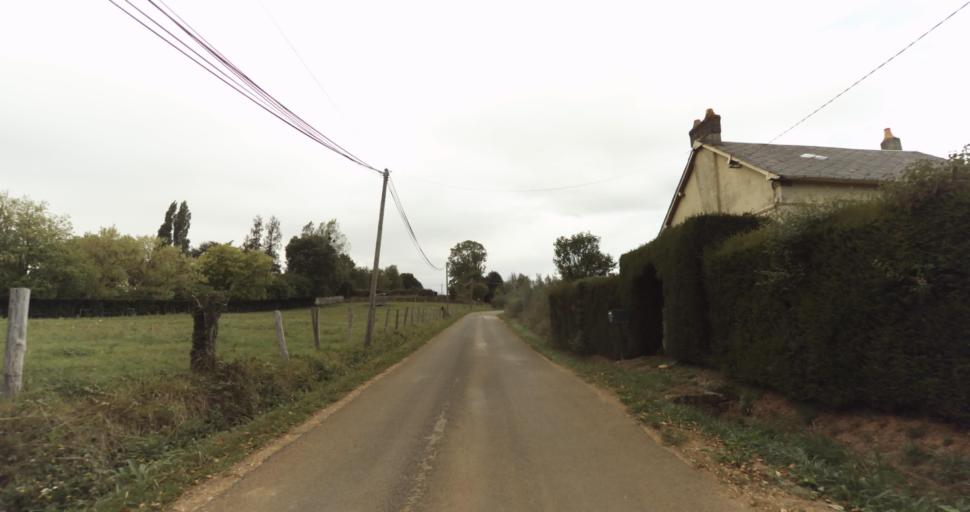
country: FR
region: Lower Normandy
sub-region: Departement de l'Orne
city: Gace
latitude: 48.7674
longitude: 0.3304
